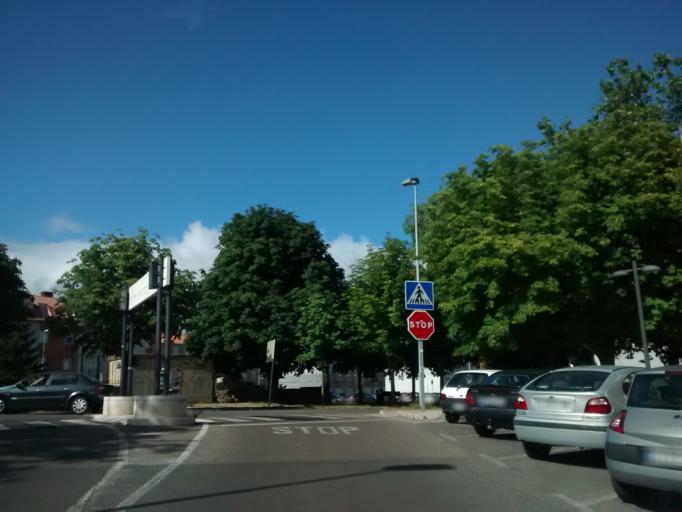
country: ES
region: Cantabria
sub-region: Provincia de Cantabria
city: Reinosa
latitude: 43.0002
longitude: -4.1421
